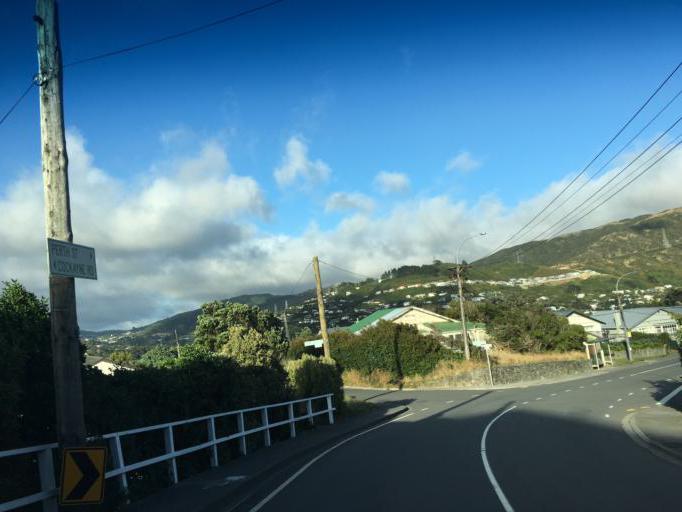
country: NZ
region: Wellington
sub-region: Wellington City
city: Kelburn
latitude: -41.2548
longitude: 174.7760
